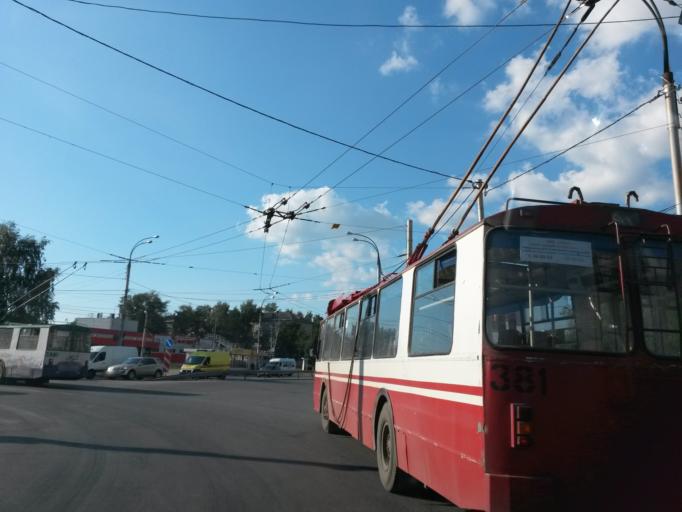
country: RU
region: Ivanovo
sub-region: Gorod Ivanovo
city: Ivanovo
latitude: 56.9646
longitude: 40.9739
